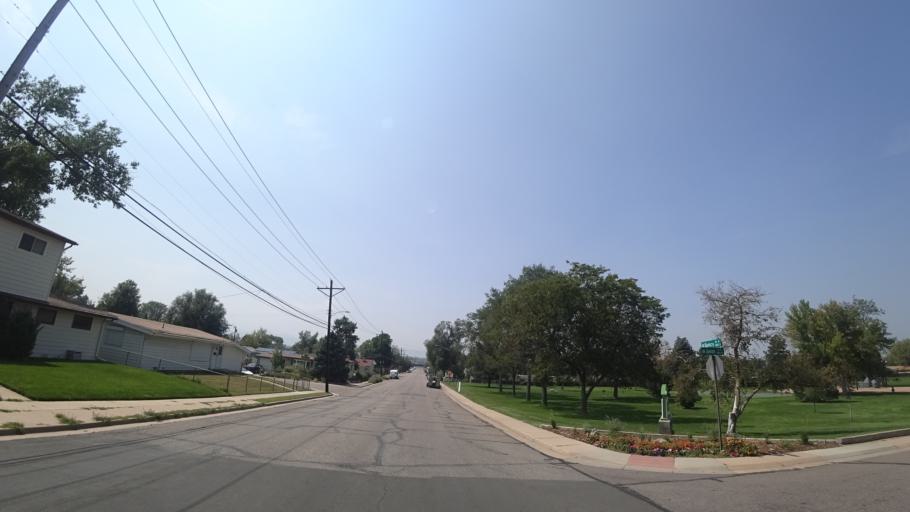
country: US
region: Colorado
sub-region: Arapahoe County
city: Englewood
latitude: 39.6386
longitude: -104.9993
